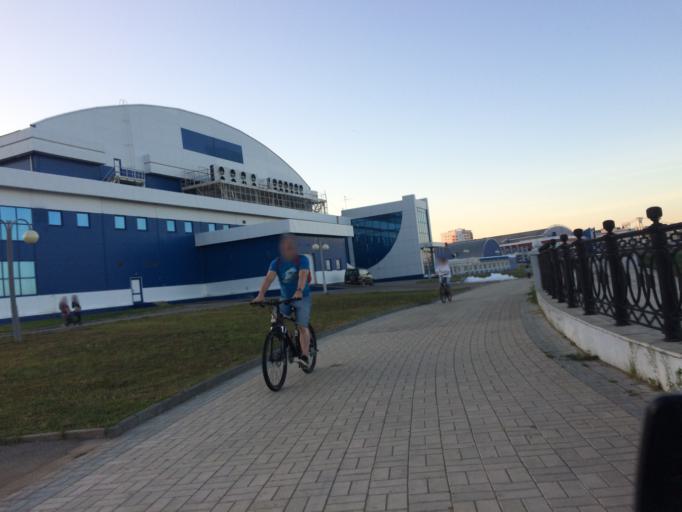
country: RU
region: Mariy-El
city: Yoshkar-Ola
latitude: 56.6237
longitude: 47.8962
